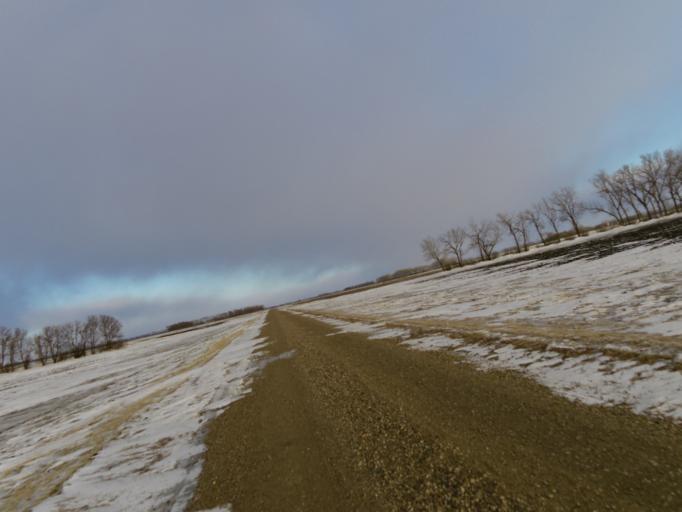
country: US
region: North Dakota
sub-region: Walsh County
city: Grafton
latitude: 48.3976
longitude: -97.2246
